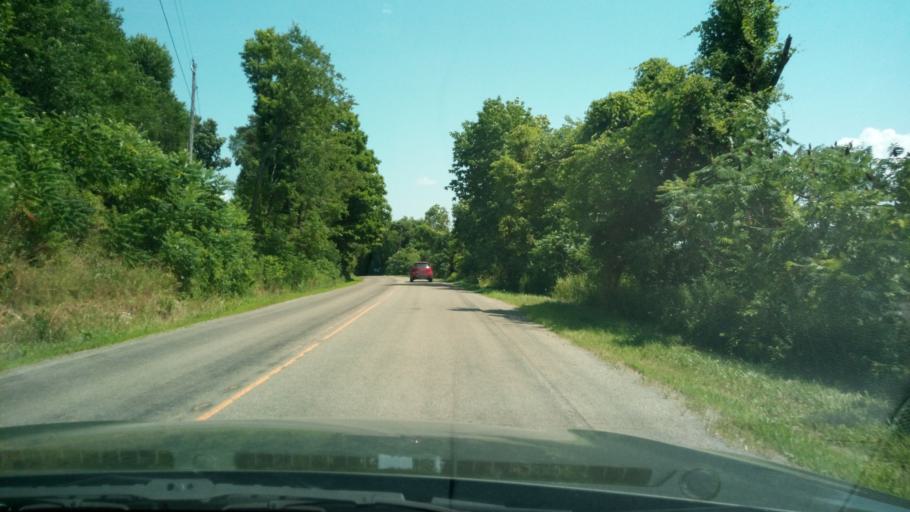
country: US
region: New York
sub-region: Schuyler County
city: Montour Falls
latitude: 42.2932
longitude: -76.7890
